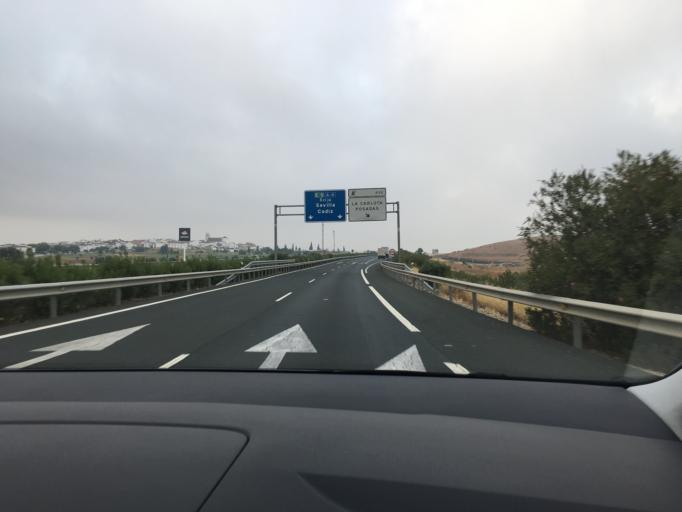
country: ES
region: Andalusia
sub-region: Province of Cordoba
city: La Carlota
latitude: 37.6819
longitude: -4.9274
